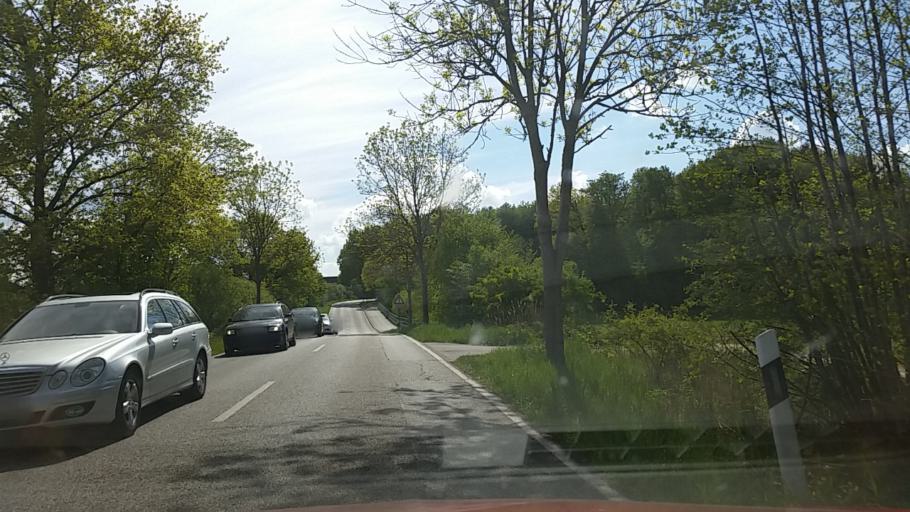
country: DE
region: Schleswig-Holstein
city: Meddewade
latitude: 53.8181
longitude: 10.4302
